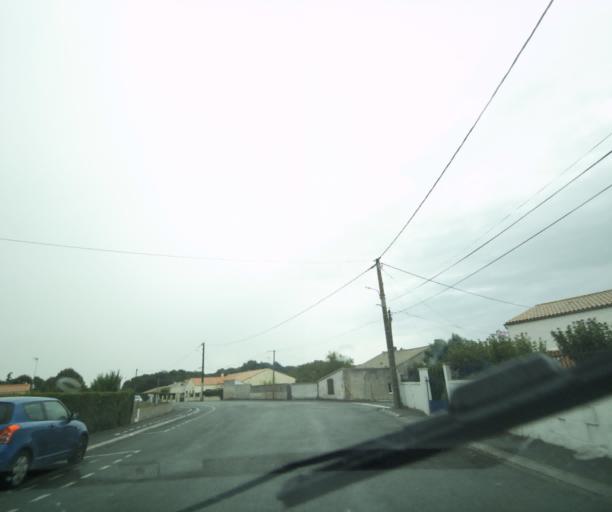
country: FR
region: Poitou-Charentes
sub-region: Departement de la Charente-Maritime
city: Tonnay-Charente
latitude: 45.9466
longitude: -0.9140
